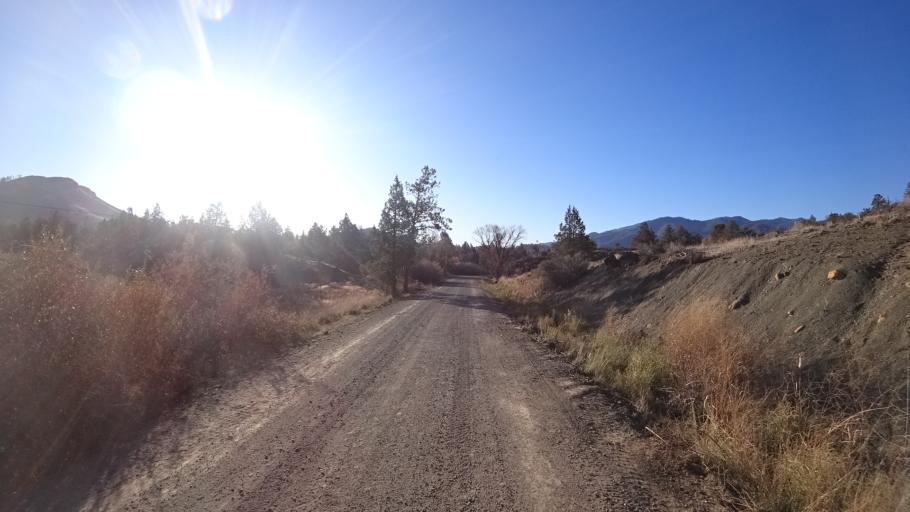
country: US
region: Oregon
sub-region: Jackson County
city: Ashland
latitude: 41.9926
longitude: -122.6238
